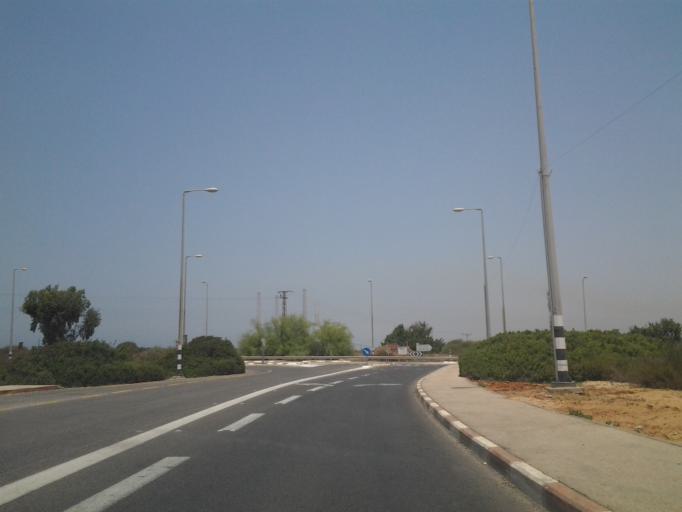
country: IL
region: Haifa
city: Hadera
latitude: 32.4455
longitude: 34.8916
